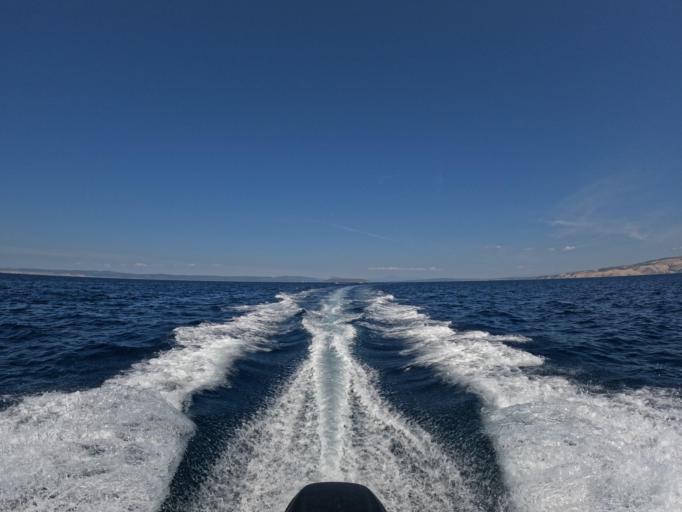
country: HR
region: Primorsko-Goranska
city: Lopar
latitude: 44.8881
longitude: 14.6477
